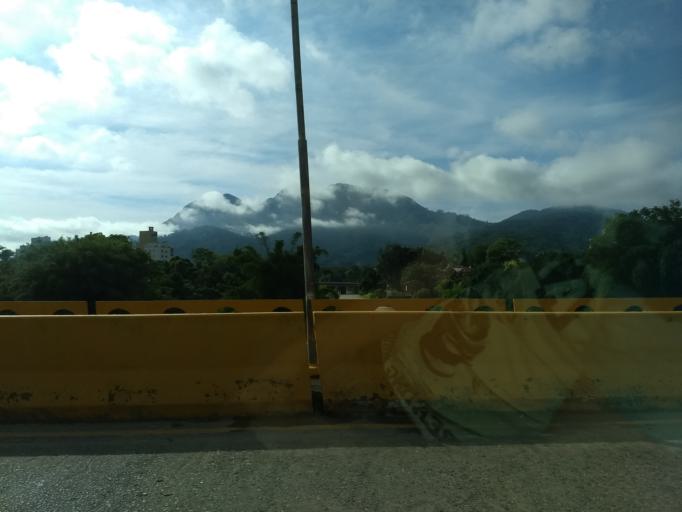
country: BR
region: Santa Catarina
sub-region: Jaragua Do Sul
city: Jaragua do Sul
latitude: -26.4827
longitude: -49.0793
